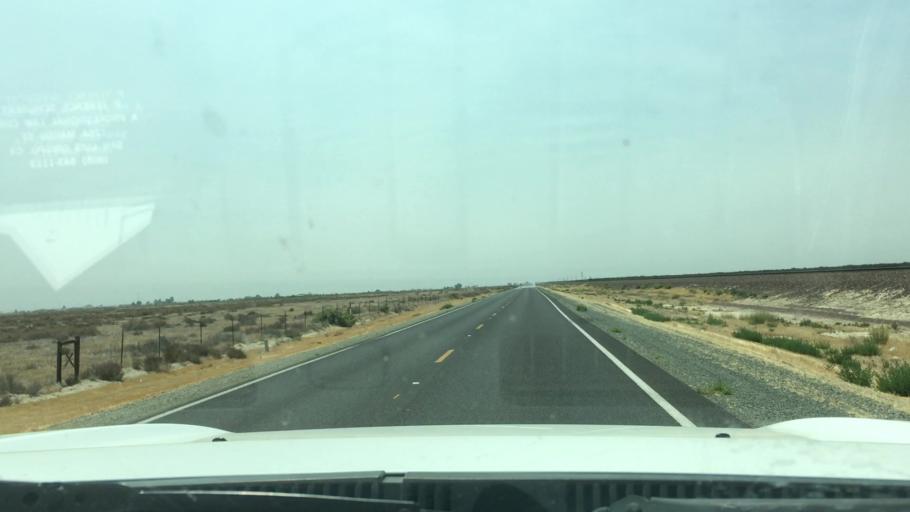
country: US
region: California
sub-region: Kern County
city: Delano
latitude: 35.7981
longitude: -119.3579
